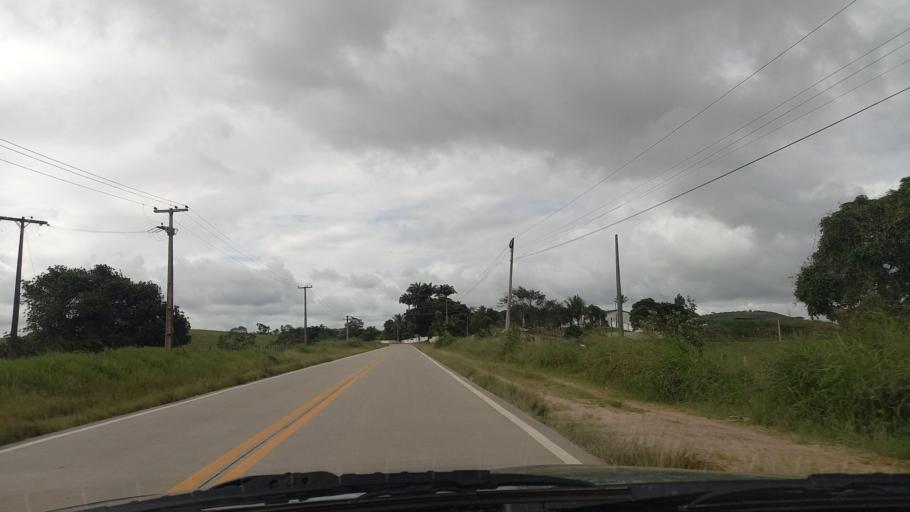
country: BR
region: Pernambuco
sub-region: Quipapa
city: Quipapa
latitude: -8.7947
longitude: -35.9942
